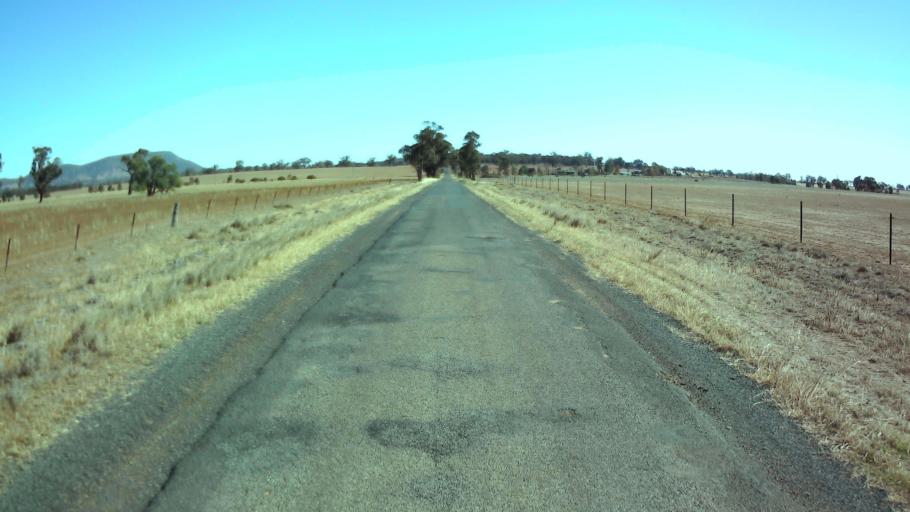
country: AU
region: New South Wales
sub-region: Weddin
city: Grenfell
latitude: -33.7981
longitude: 147.9562
